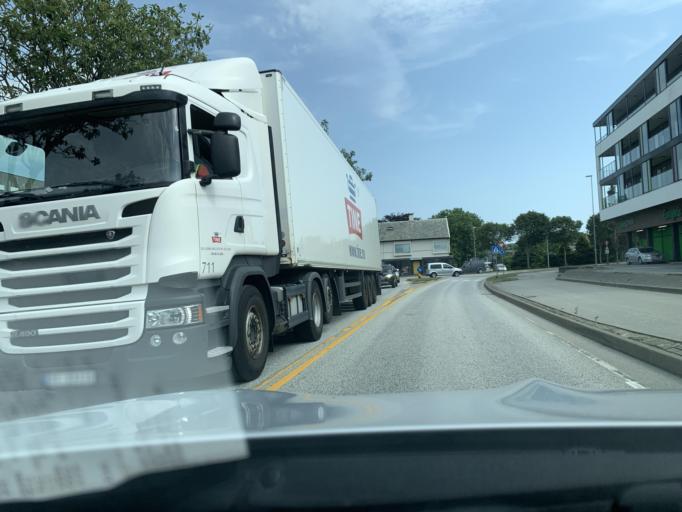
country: NO
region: Rogaland
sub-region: Klepp
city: Kleppe
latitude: 58.7764
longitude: 5.6293
